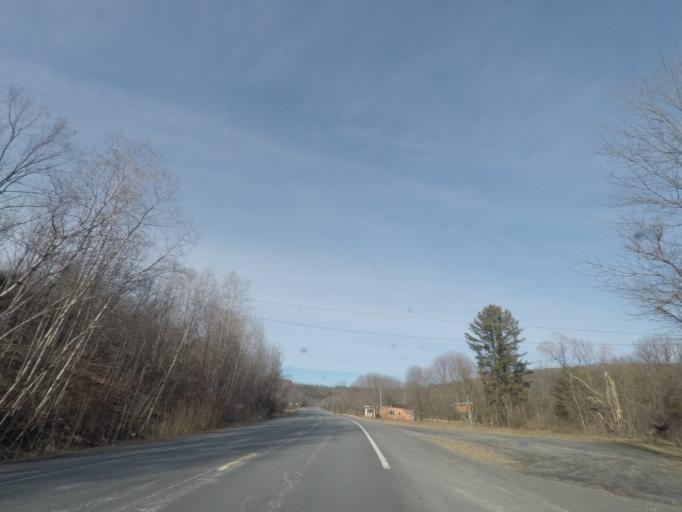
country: US
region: Massachusetts
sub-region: Berkshire County
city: Williamstown
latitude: 42.7316
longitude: -73.3623
